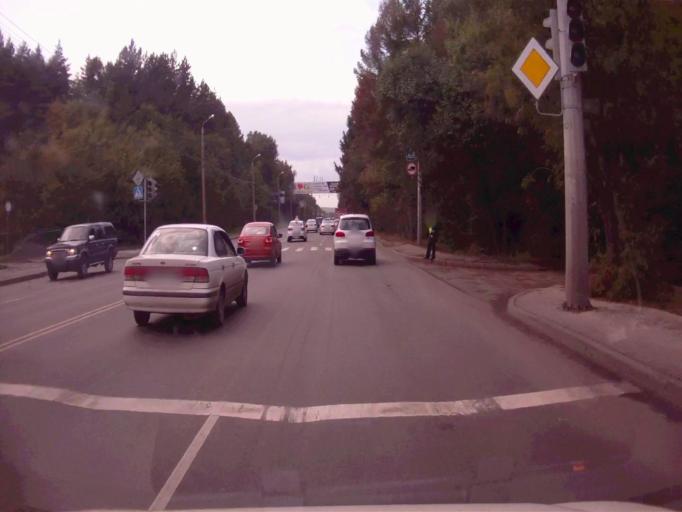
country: RU
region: Chelyabinsk
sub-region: Gorod Chelyabinsk
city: Chelyabinsk
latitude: 55.1471
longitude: 61.3536
